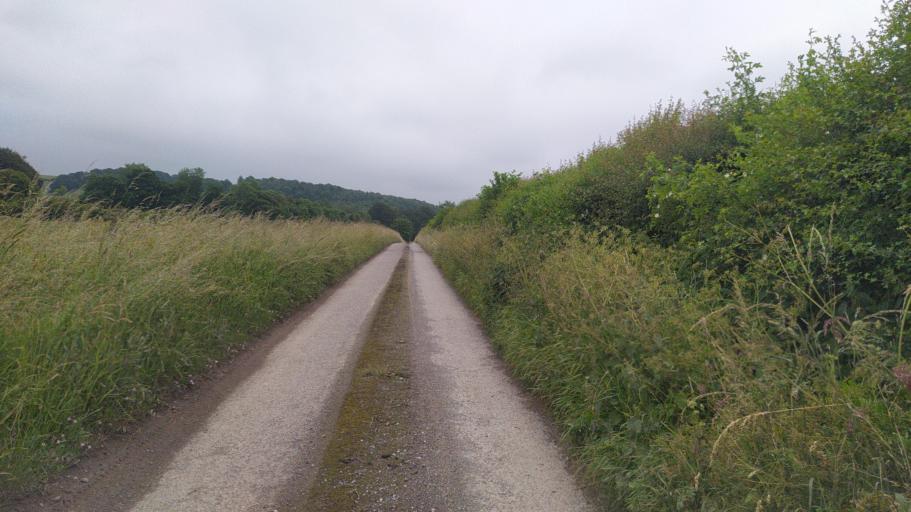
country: GB
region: England
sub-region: Wiltshire
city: Bishopstrow
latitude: 51.1986
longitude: -2.1041
